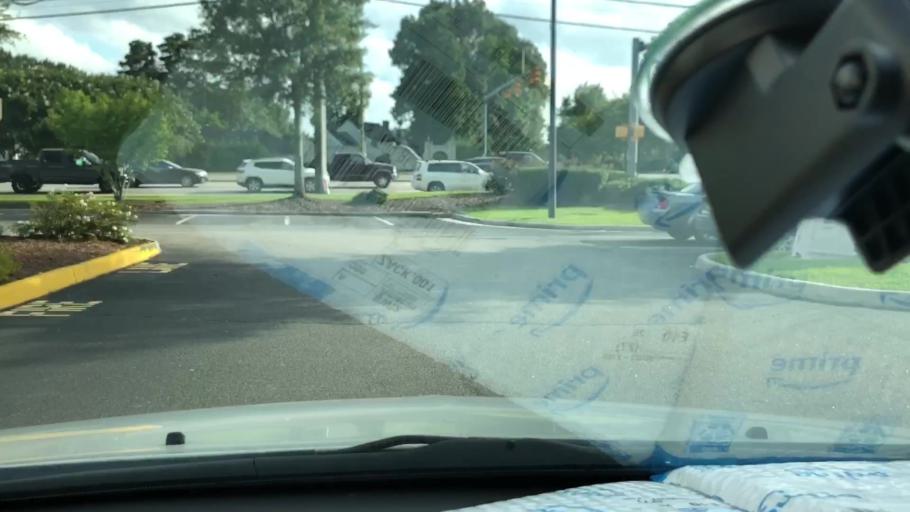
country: US
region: Virginia
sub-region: City of Chesapeake
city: Chesapeake
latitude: 36.7123
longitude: -76.2766
